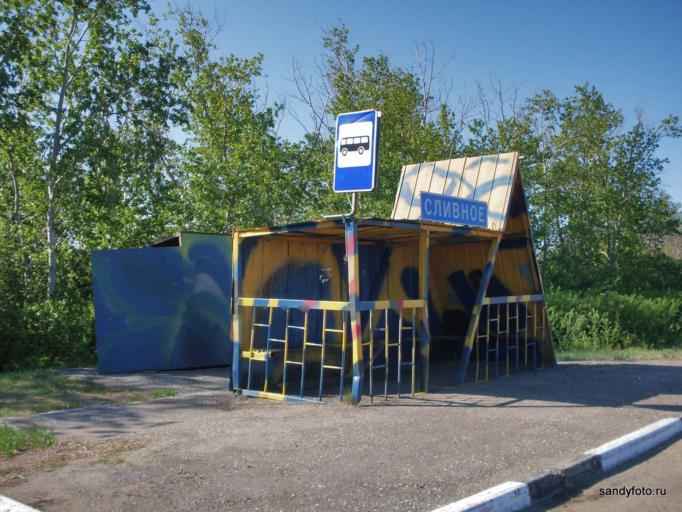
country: RU
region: Chelyabinsk
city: Bobrovka
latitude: 54.1337
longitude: 61.7055
